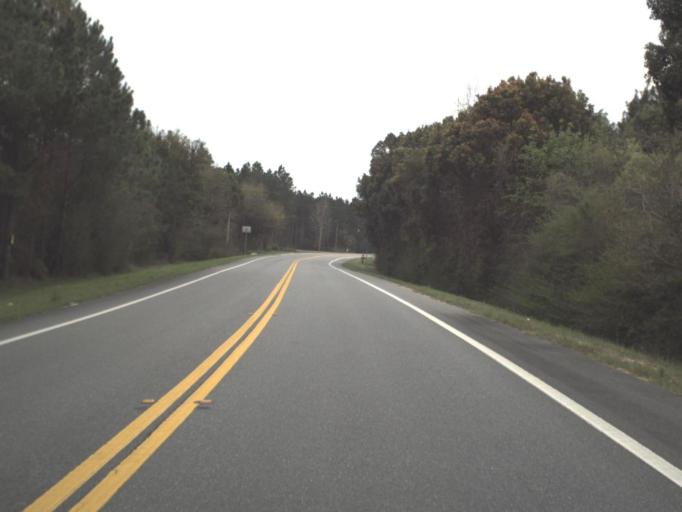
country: US
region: Florida
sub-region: Gulf County
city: Wewahitchka
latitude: 30.2021
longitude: -85.2086
